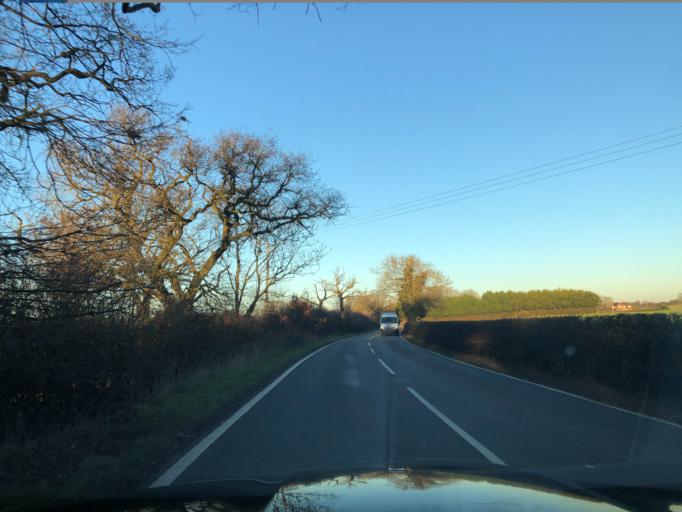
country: GB
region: England
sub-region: Warwickshire
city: Harbury
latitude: 52.2001
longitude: -1.4514
